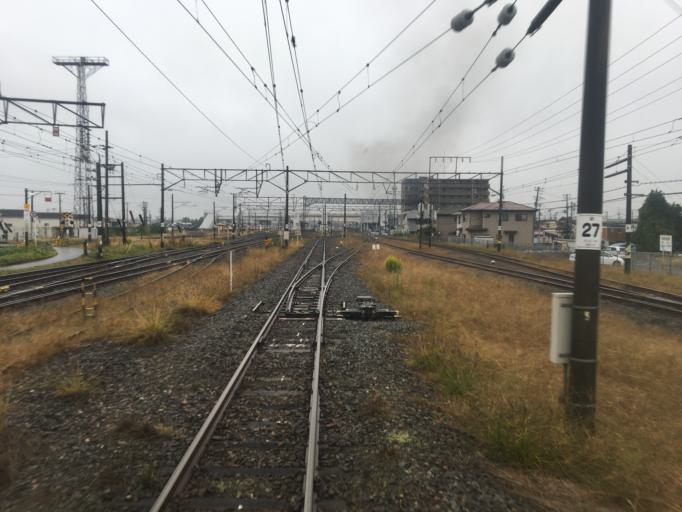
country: JP
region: Miyagi
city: Kogota
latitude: 38.5442
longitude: 141.0639
